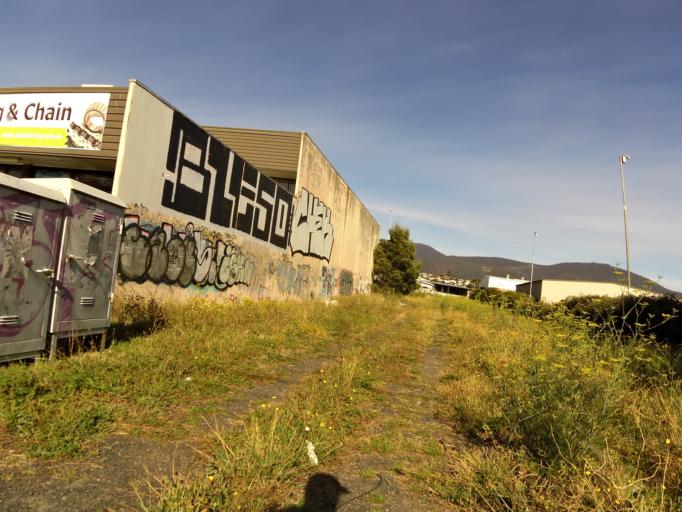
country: AU
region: Tasmania
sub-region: Glenorchy
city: Goodwood
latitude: -42.8379
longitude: 147.2935
